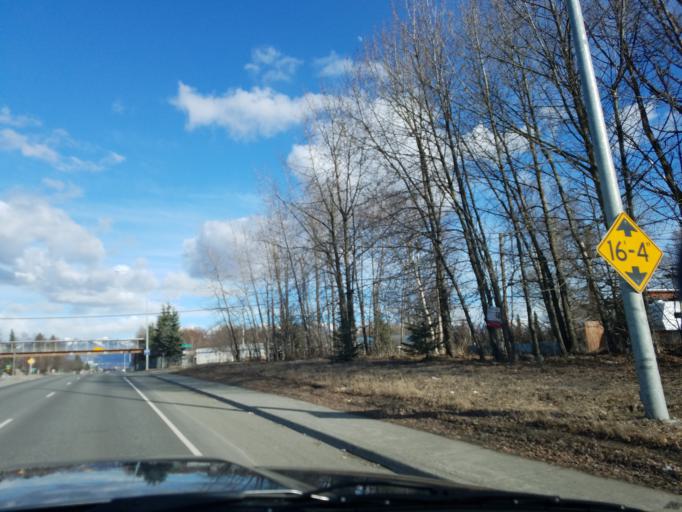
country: US
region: Alaska
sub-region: Anchorage Municipality
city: Anchorage
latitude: 61.1806
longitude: -149.9068
